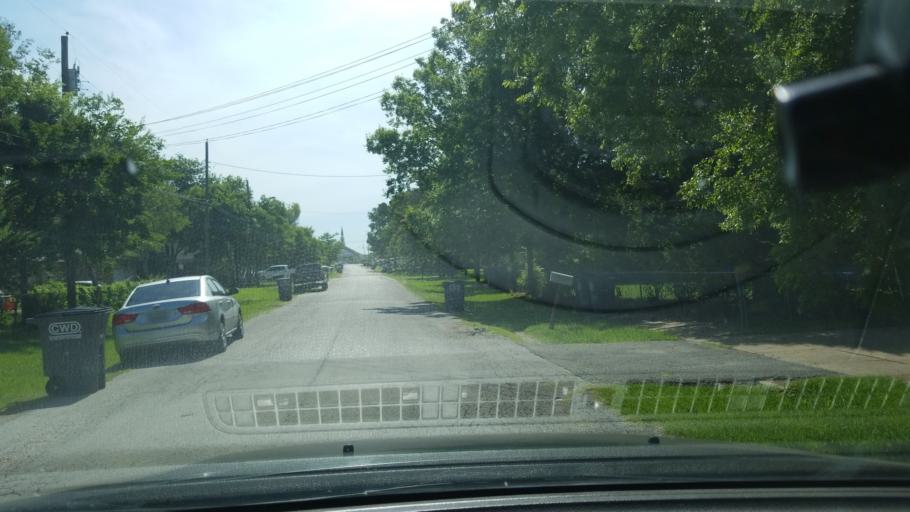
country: US
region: Texas
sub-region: Dallas County
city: Balch Springs
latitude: 32.7261
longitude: -96.6261
